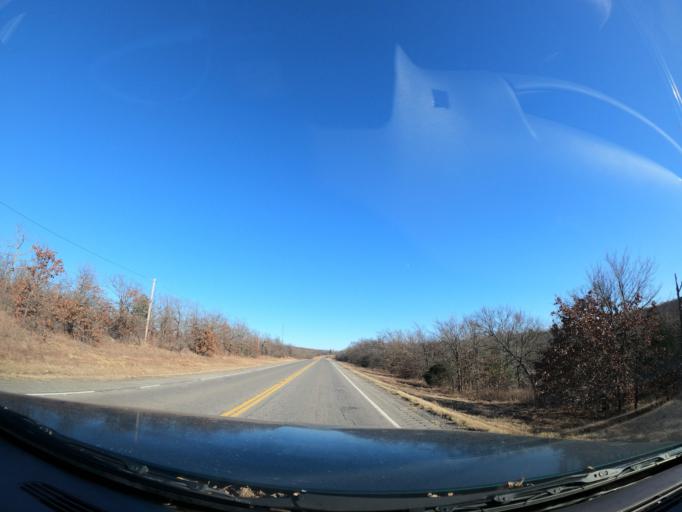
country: US
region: Oklahoma
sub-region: Pittsburg County
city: Longtown
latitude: 35.2252
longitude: -95.4397
